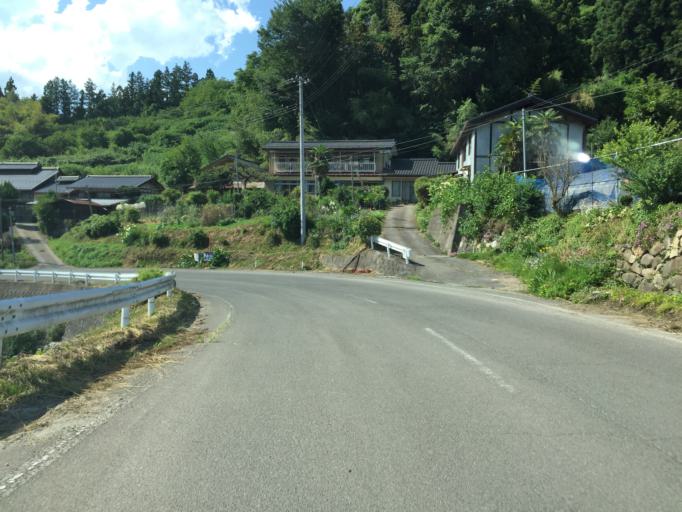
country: JP
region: Fukushima
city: Yanagawamachi-saiwaicho
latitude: 37.7895
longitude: 140.6516
